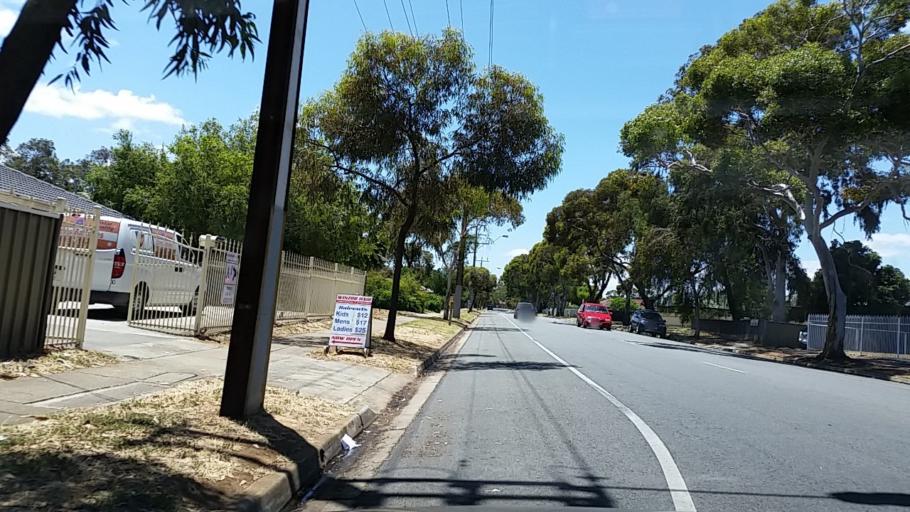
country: AU
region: South Australia
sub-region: Salisbury
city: Salisbury
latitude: -34.7656
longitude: 138.6265
